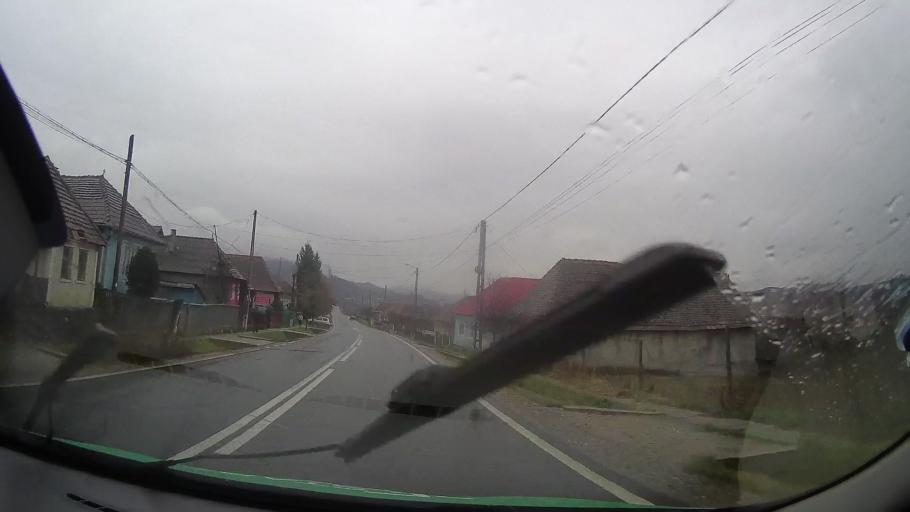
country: RO
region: Bistrita-Nasaud
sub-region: Comuna Galatii Bistritei
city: Galatii Bistritei
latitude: 46.9903
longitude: 24.4223
